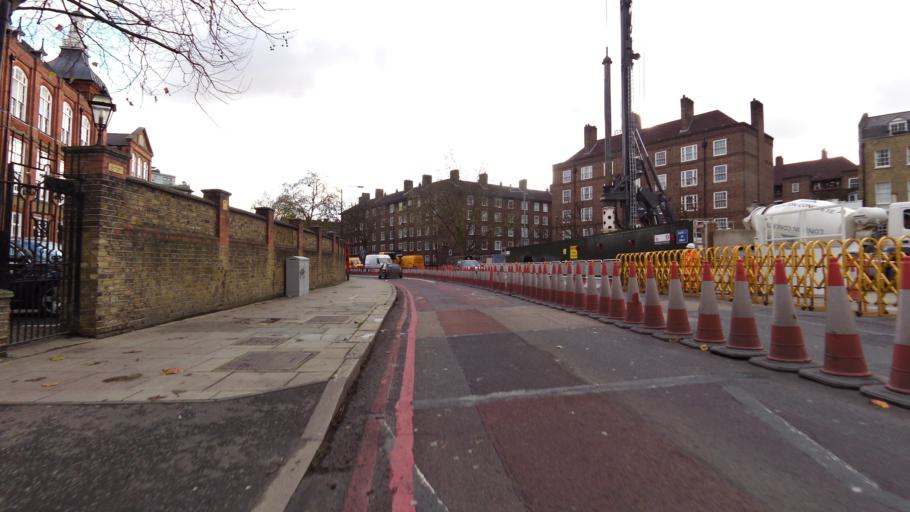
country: GB
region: England
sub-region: Greater London
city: Kennington
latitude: 51.4860
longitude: -0.1112
